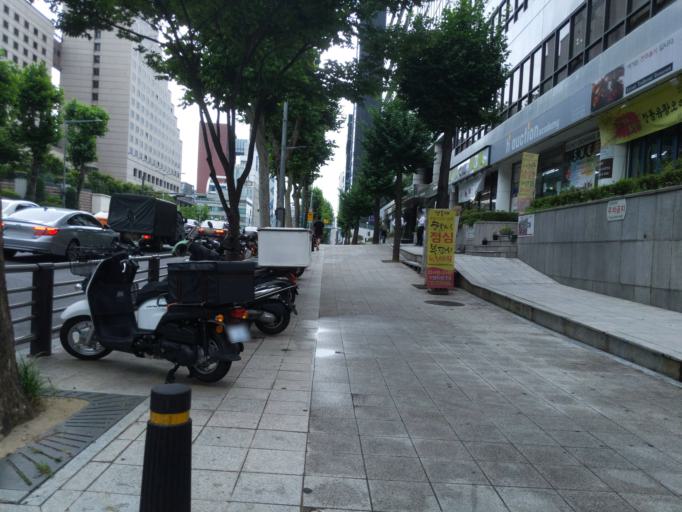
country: KR
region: Seoul
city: Seoul
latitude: 37.5059
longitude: 127.0289
